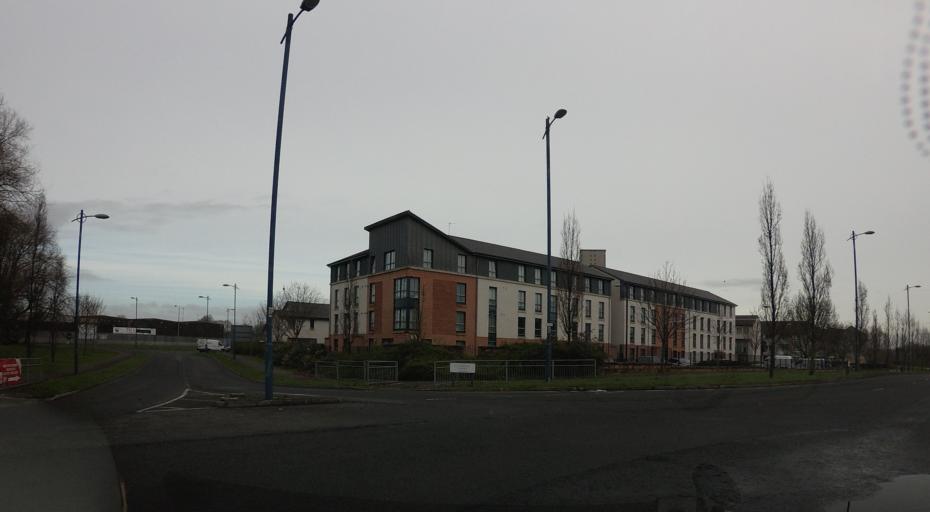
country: GB
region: Scotland
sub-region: Glasgow City
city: Glasgow
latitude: 55.8409
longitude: -4.2439
